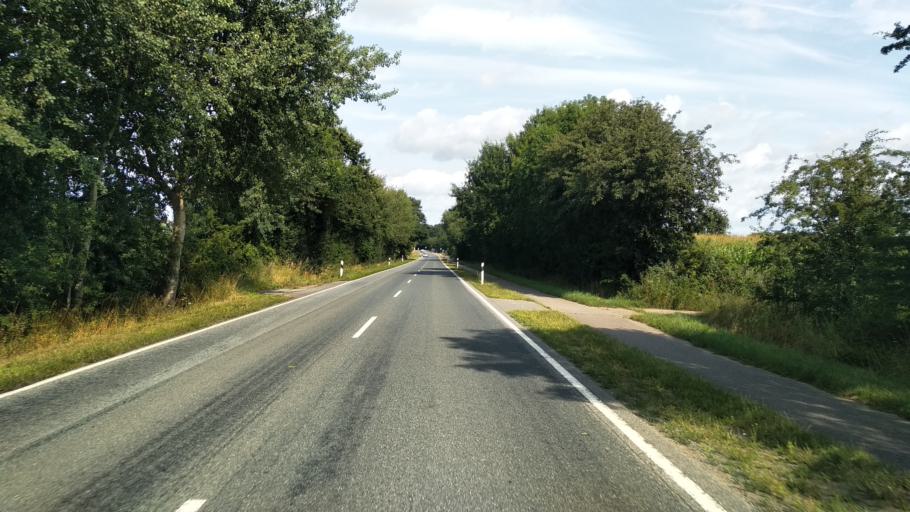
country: DE
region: Schleswig-Holstein
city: Selk
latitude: 54.4808
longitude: 9.5657
